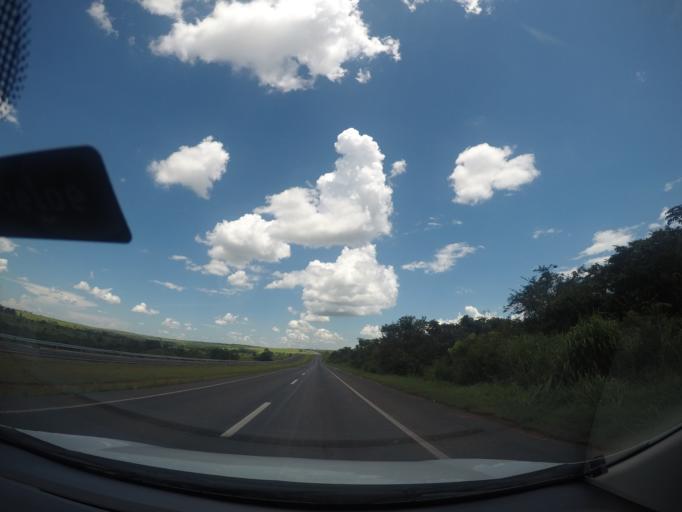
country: BR
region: Minas Gerais
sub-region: Prata
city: Prata
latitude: -19.4240
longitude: -48.8892
